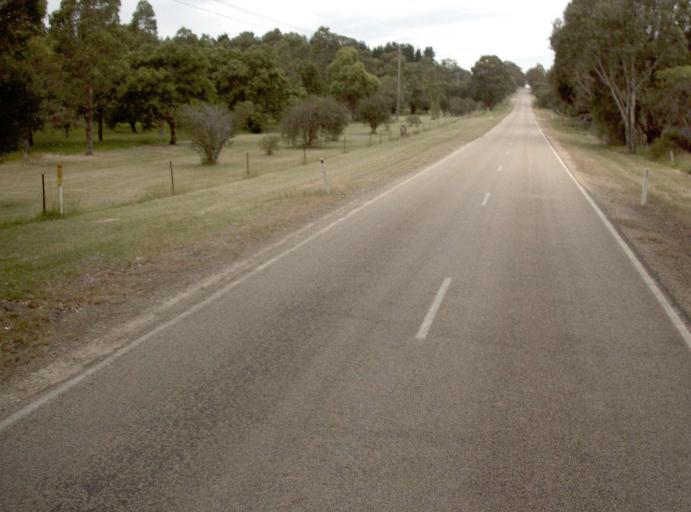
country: AU
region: Victoria
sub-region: East Gippsland
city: Bairnsdale
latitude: -37.8342
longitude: 147.4327
